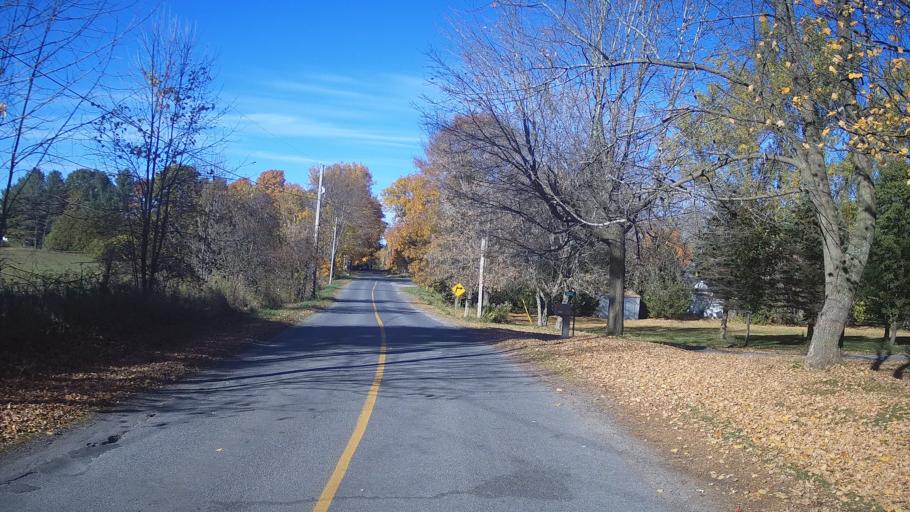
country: CA
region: Ontario
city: Kingston
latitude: 44.4466
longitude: -76.5174
